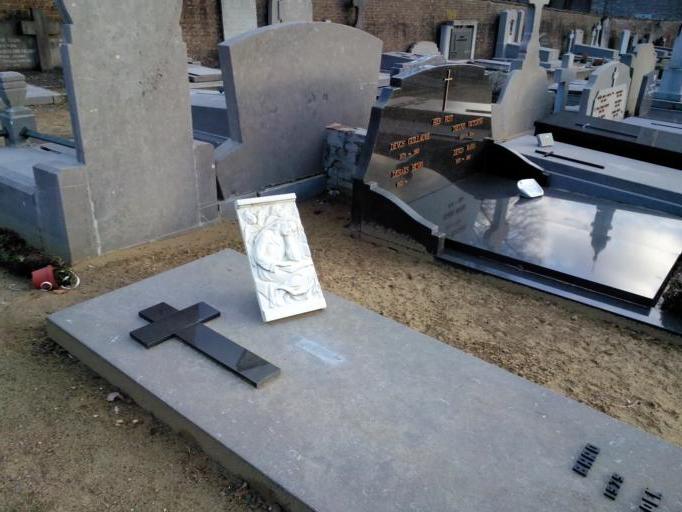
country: BE
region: Flanders
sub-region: Provincie Vlaams-Brabant
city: Leuven
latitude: 50.8655
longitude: 4.7177
